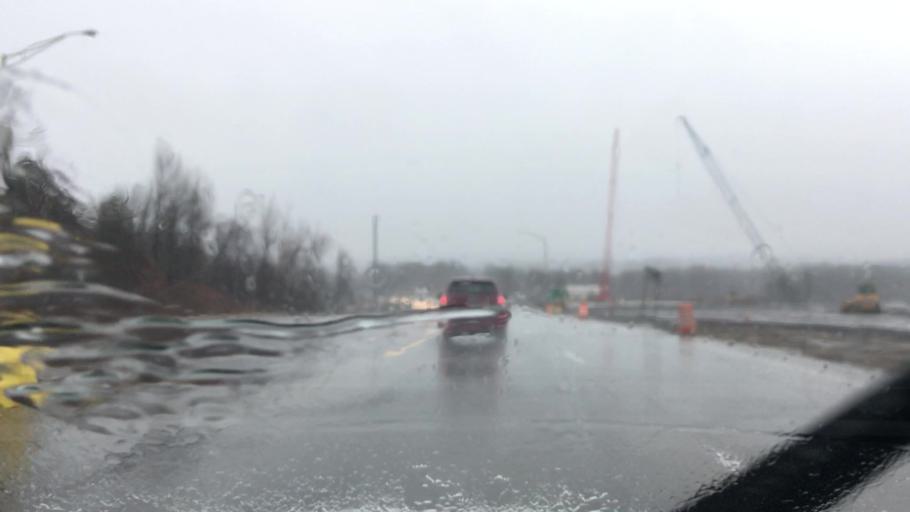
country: US
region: New Hampshire
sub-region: Rockingham County
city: Derry
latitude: 42.8689
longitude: -71.3430
